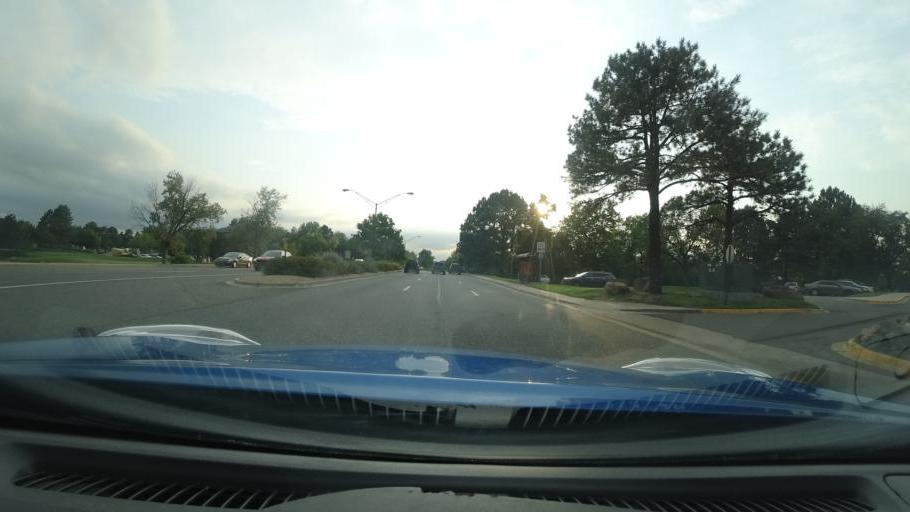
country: US
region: Colorado
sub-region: Adams County
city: Aurora
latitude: 39.6750
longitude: -104.8334
